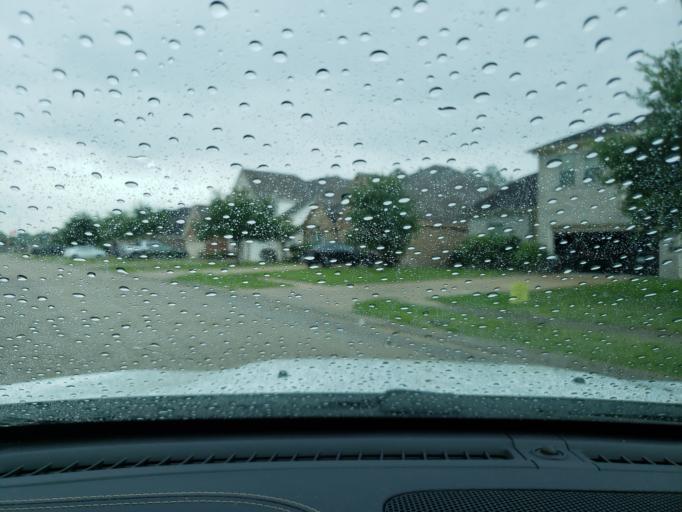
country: US
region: Texas
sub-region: Chambers County
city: Mont Belvieu
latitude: 29.8053
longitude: -94.9072
